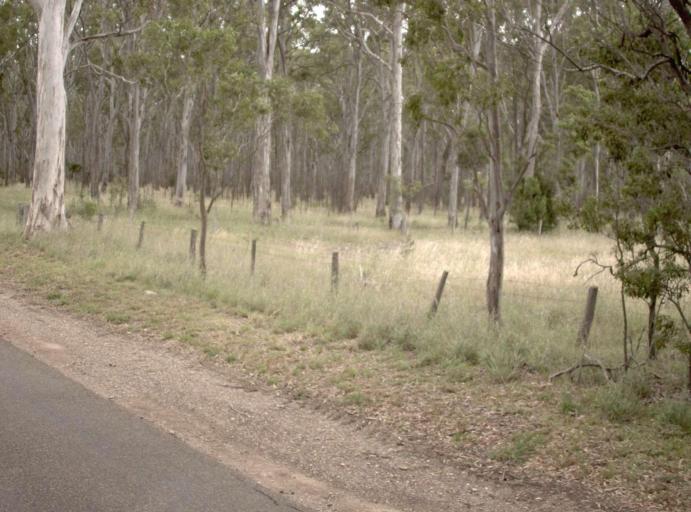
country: AU
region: Victoria
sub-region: Wellington
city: Sale
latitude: -37.8623
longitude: 147.0689
